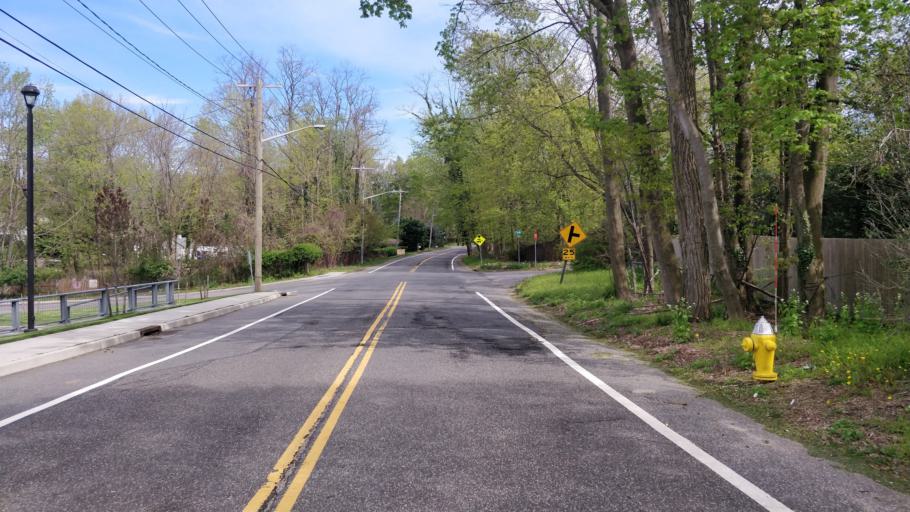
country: US
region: New York
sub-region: Suffolk County
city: East Setauket
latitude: 40.9406
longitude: -73.1050
